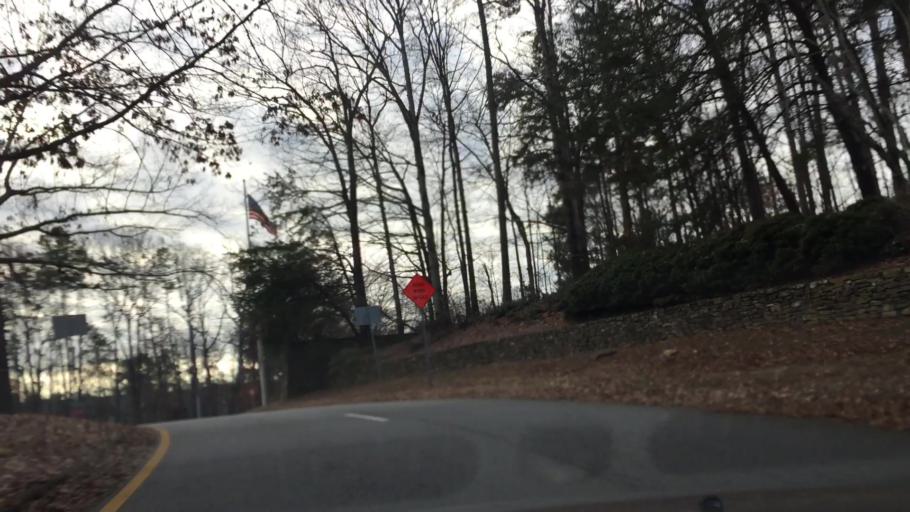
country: US
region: Georgia
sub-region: DeKalb County
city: Dunwoody
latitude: 33.9741
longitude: -84.3576
